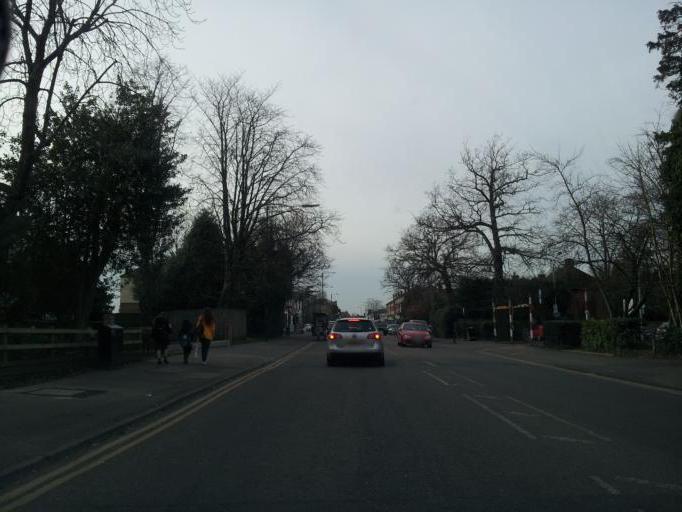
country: GB
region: England
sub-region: Hertfordshire
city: Bushey
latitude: 51.6339
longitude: -0.3411
